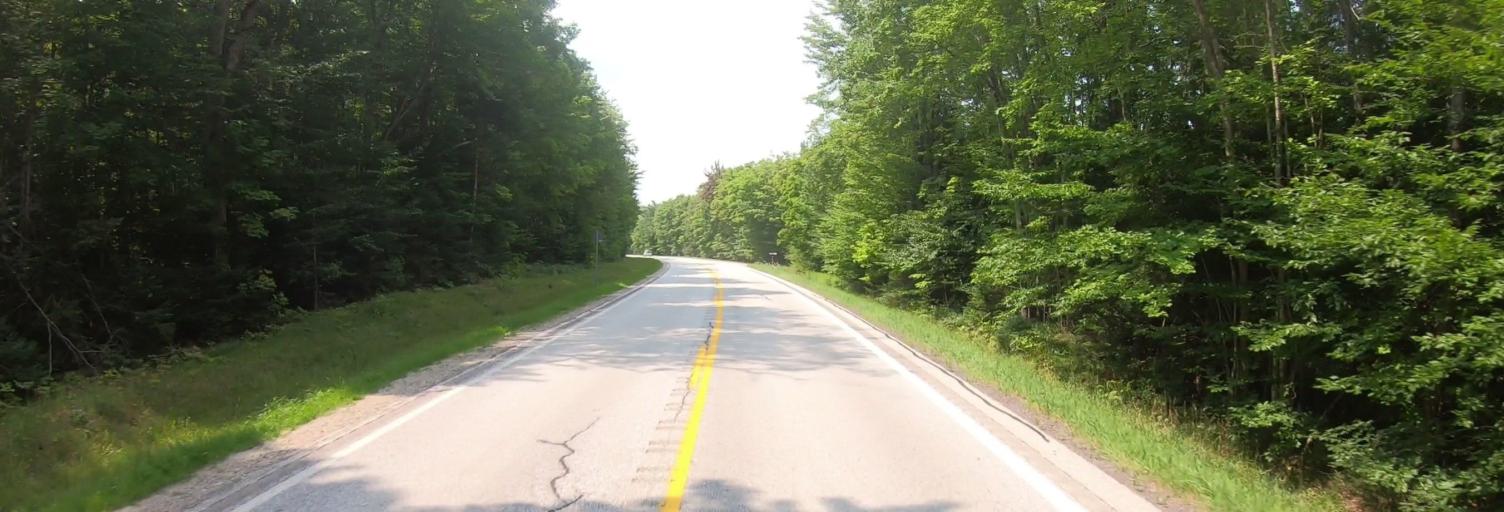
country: US
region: Michigan
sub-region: Luce County
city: Newberry
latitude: 46.5152
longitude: -85.4237
